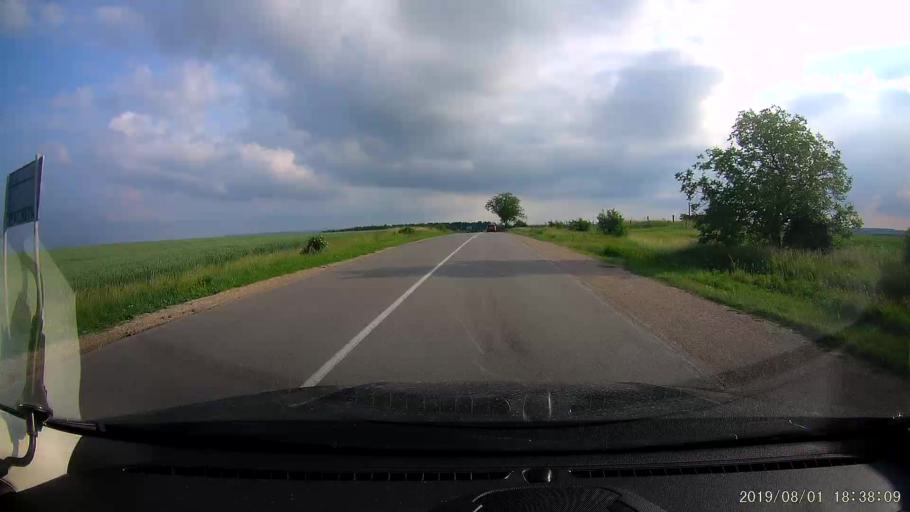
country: BG
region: Shumen
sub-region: Obshtina Khitrino
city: Gara Khitrino
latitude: 43.4068
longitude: 26.9203
